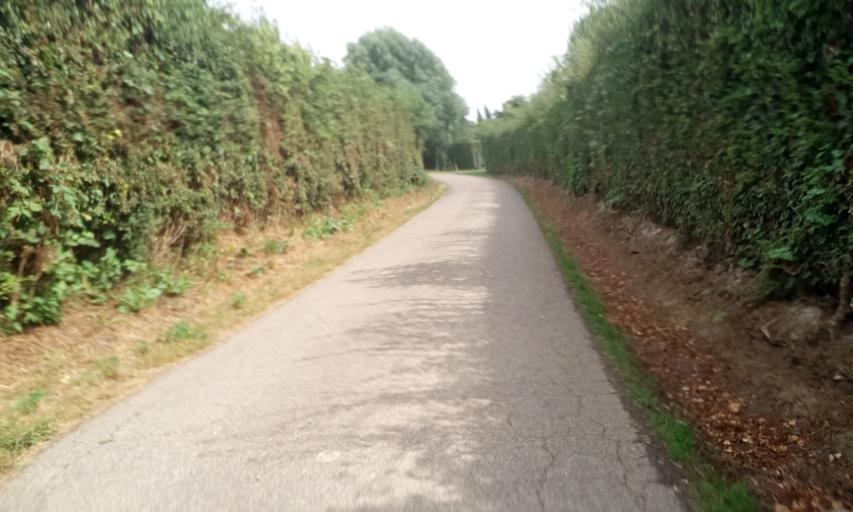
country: FR
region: Lower Normandy
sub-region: Departement du Calvados
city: Bavent
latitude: 49.2495
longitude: -0.1916
